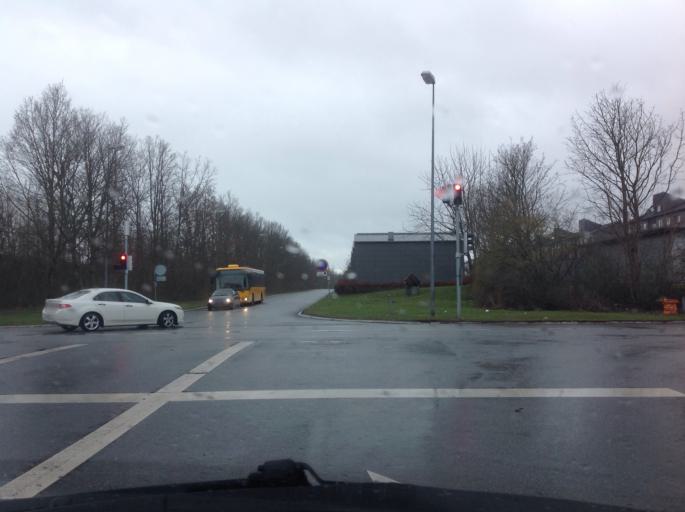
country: DK
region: Capital Region
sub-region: Ishoj Kommune
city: Ishoj
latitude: 55.6124
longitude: 12.3563
